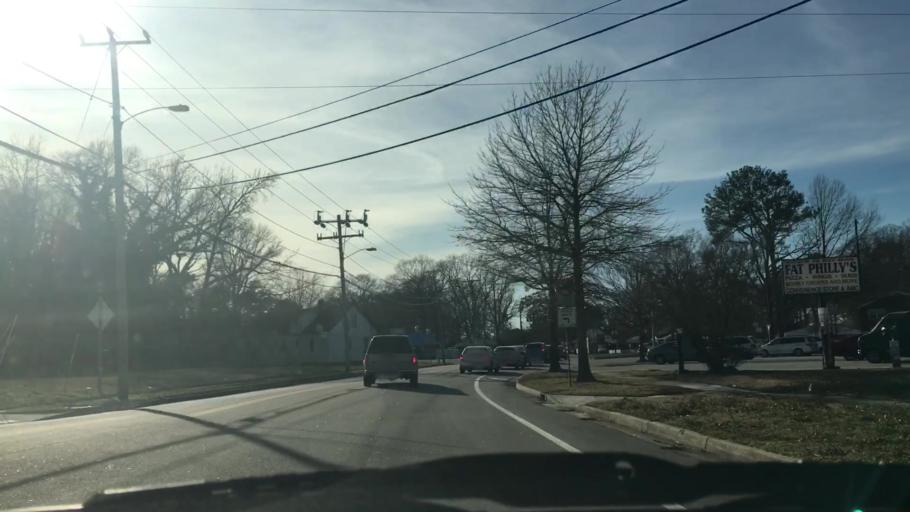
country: US
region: Virginia
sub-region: City of Norfolk
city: Norfolk
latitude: 36.8793
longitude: -76.2256
